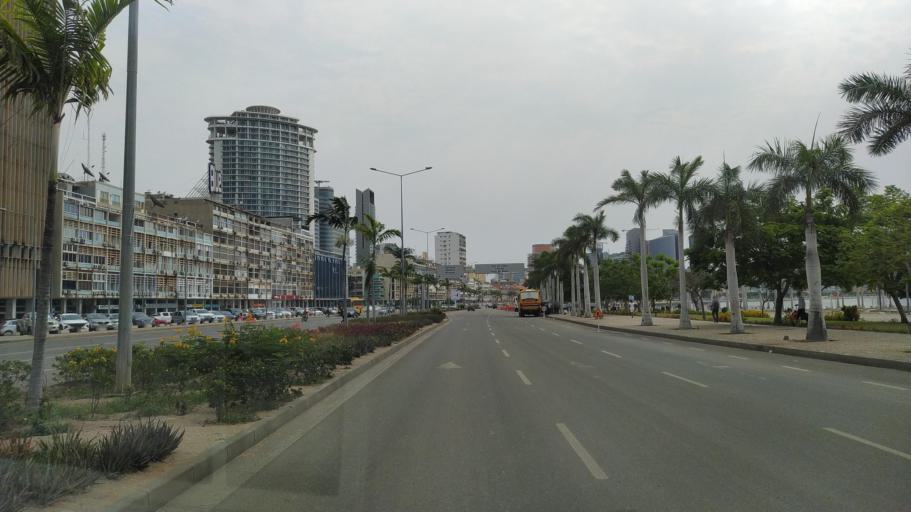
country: AO
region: Luanda
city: Luanda
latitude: -8.8051
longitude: 13.2403
